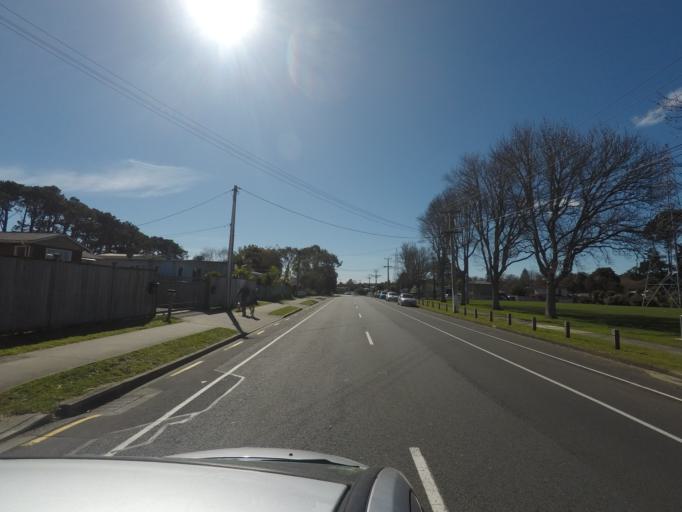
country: NZ
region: Auckland
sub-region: Auckland
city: Waitakere
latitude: -36.9219
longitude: 174.6911
